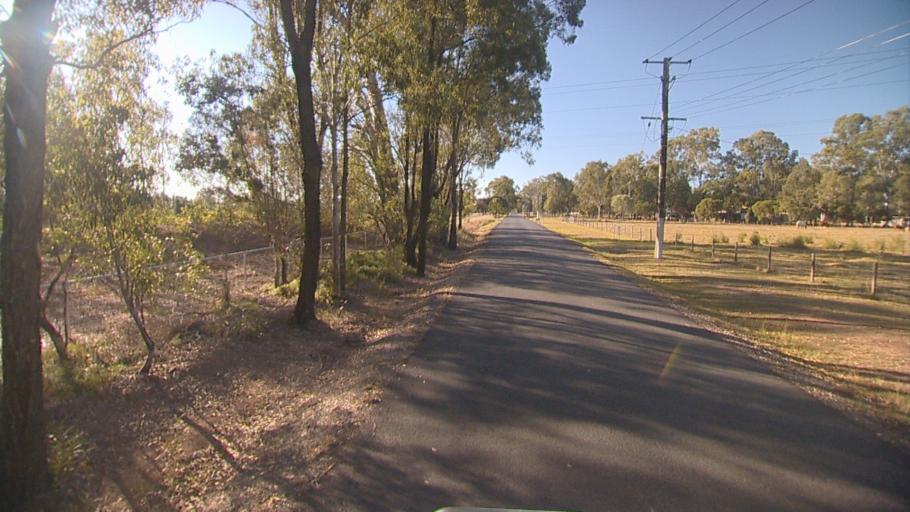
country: AU
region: Queensland
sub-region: Logan
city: North Maclean
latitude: -27.7793
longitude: 153.0468
